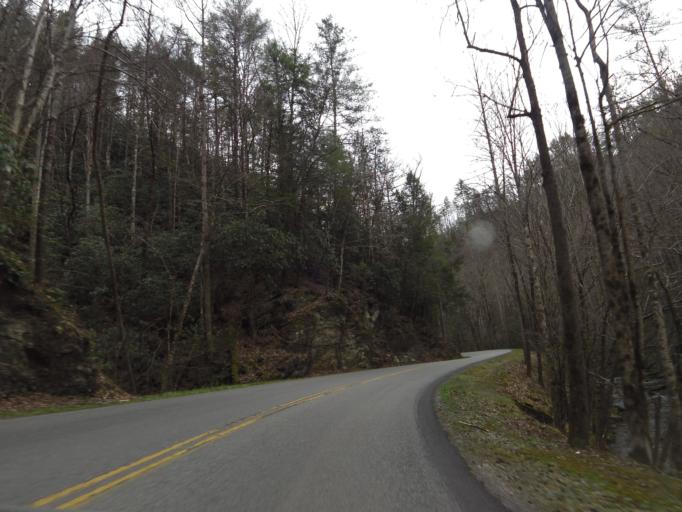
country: US
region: Tennessee
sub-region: Sevier County
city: Gatlinburg
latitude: 35.6451
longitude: -83.7169
